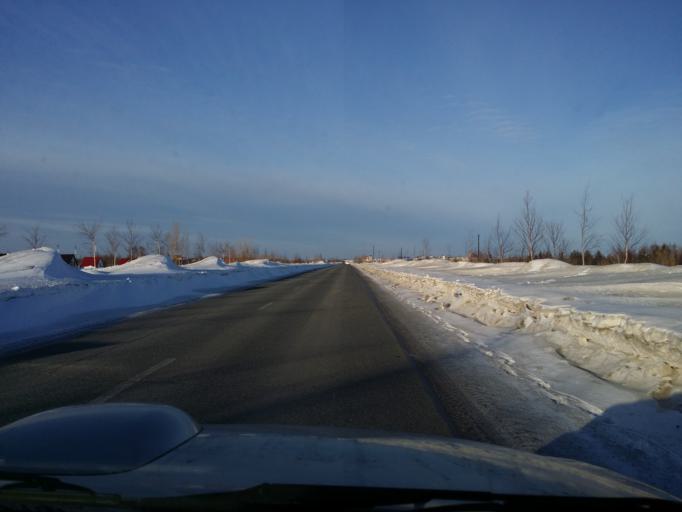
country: RU
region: Khanty-Mansiyskiy Avtonomnyy Okrug
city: Izluchinsk
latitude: 60.9712
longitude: 76.8913
